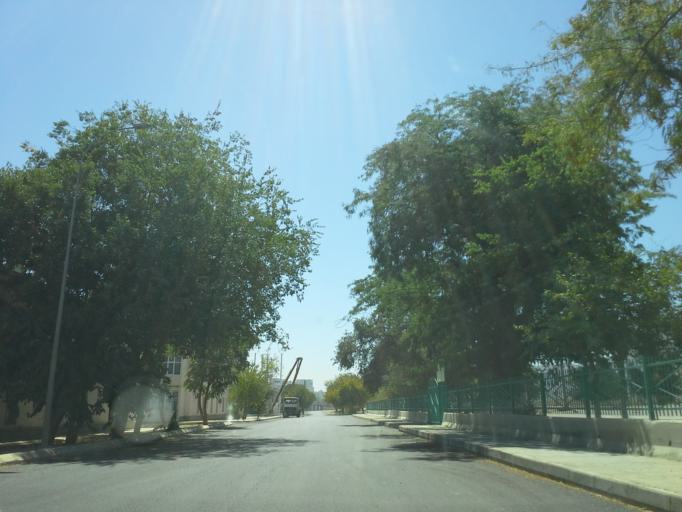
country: TM
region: Ahal
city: Ashgabat
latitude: 37.9460
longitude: 58.3508
